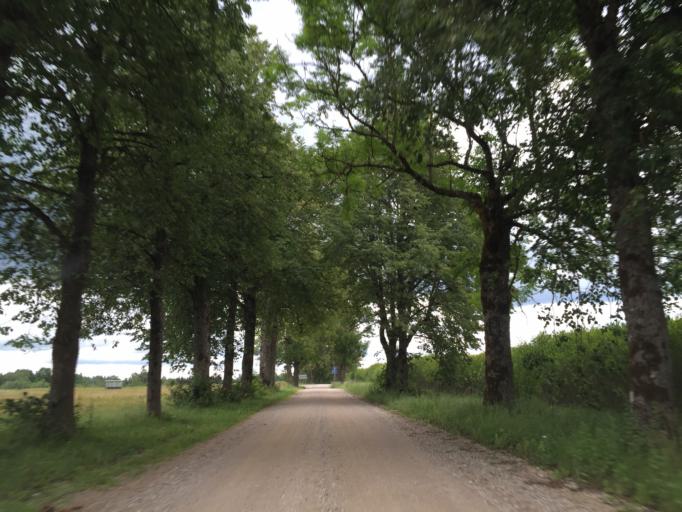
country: LV
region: Malpils
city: Malpils
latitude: 56.9235
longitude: 25.0065
